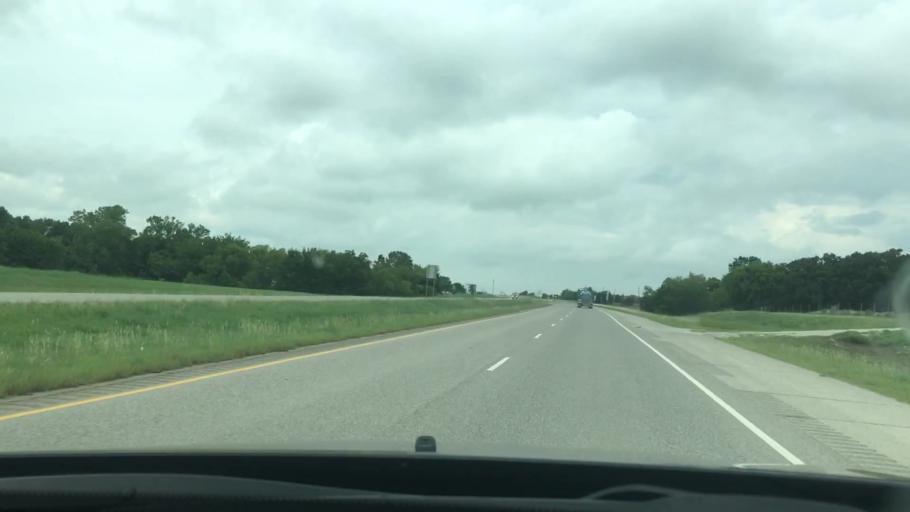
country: US
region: Oklahoma
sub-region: Carter County
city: Wilson
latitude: 34.1734
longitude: -97.4277
